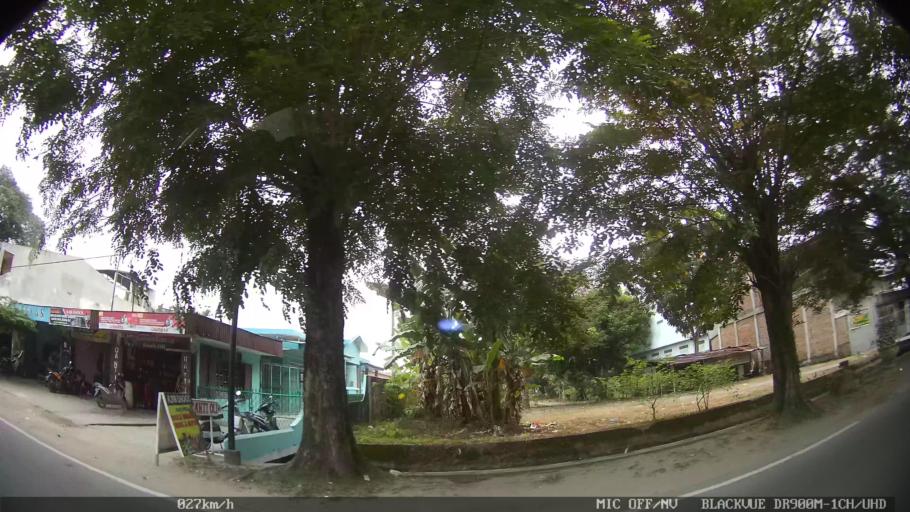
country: ID
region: North Sumatra
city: Medan
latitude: 3.5683
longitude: 98.7116
